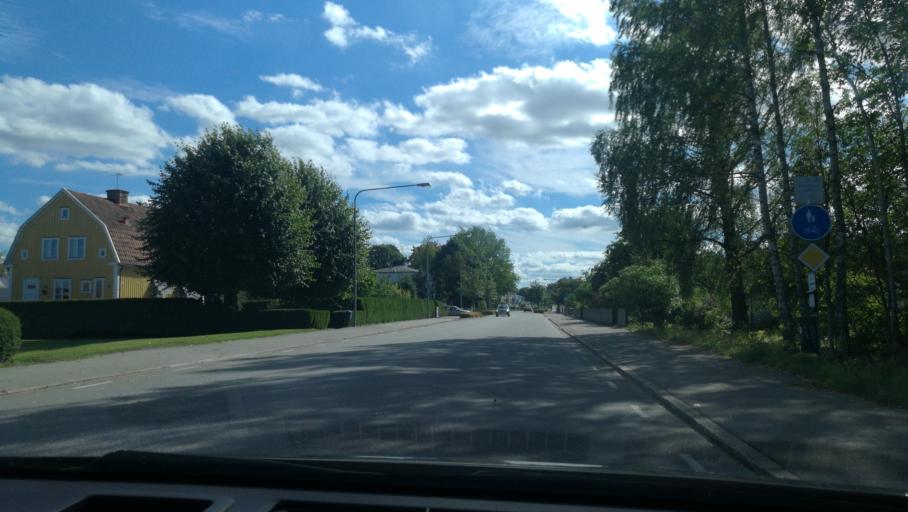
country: SE
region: Vaestra Goetaland
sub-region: Mariestads Kommun
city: Mariestad
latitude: 58.6984
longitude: 13.8371
